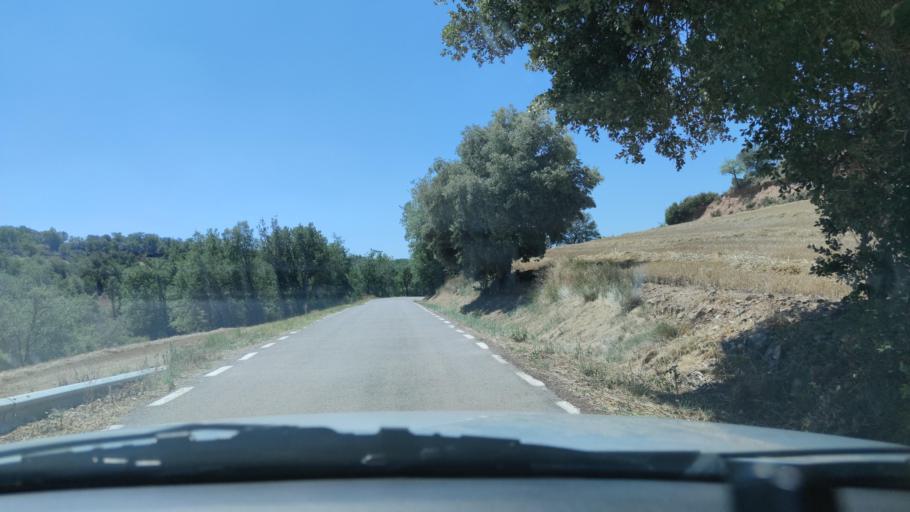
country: ES
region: Catalonia
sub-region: Provincia de Lleida
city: Tora de Riubregos
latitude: 41.8442
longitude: 1.4241
